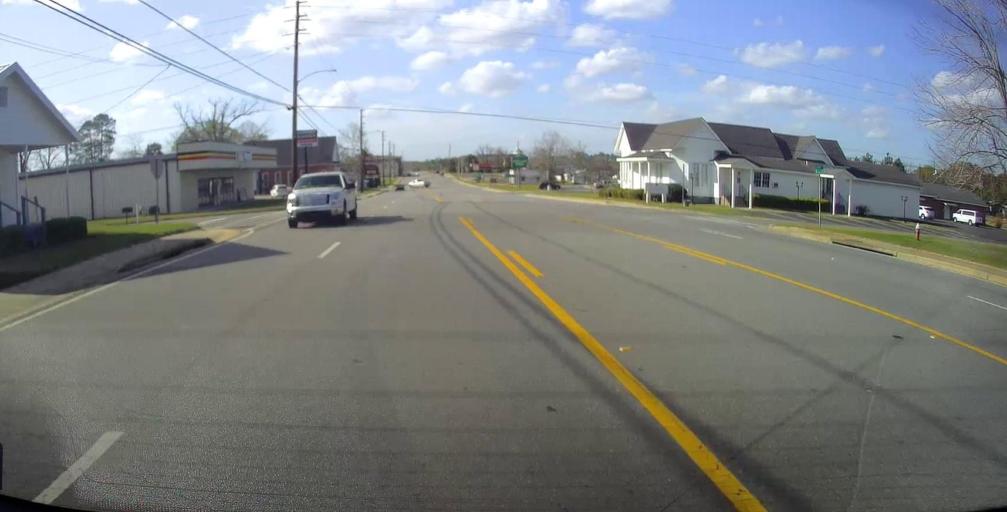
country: US
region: Georgia
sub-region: Telfair County
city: Helena
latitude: 32.0714
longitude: -82.9112
